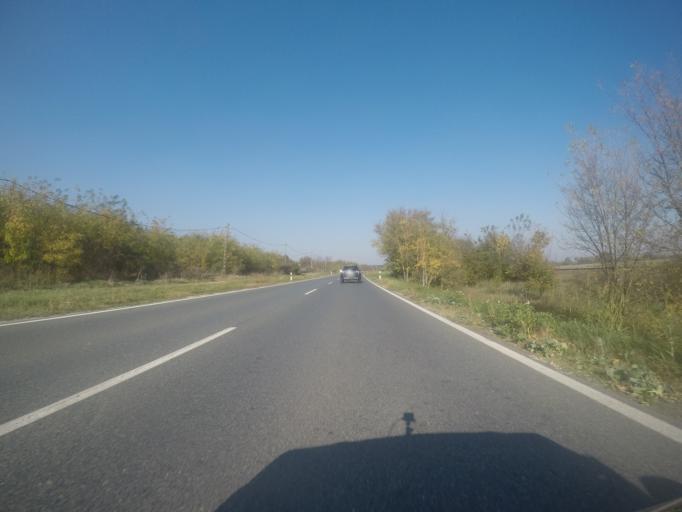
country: HU
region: Tolna
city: Paks
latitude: 46.6750
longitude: 18.8815
